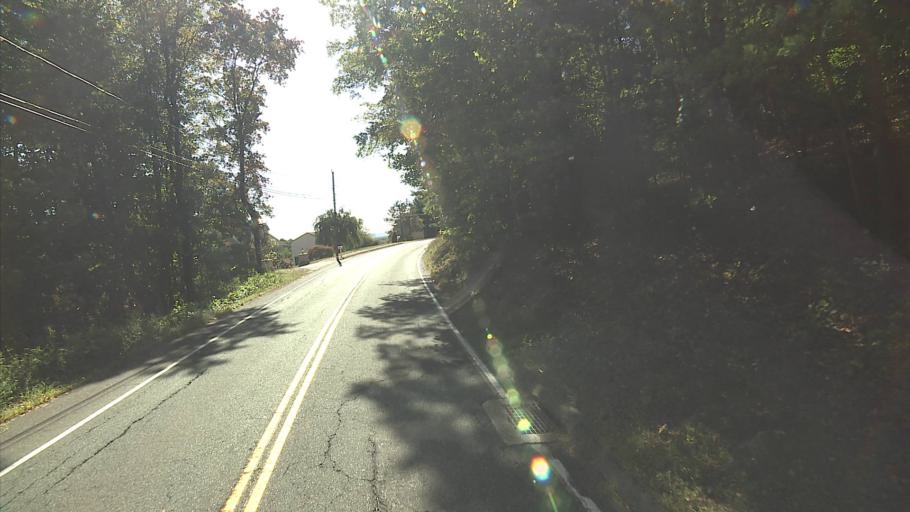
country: US
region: Connecticut
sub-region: Hartford County
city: Bristol
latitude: 41.7288
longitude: -72.9510
